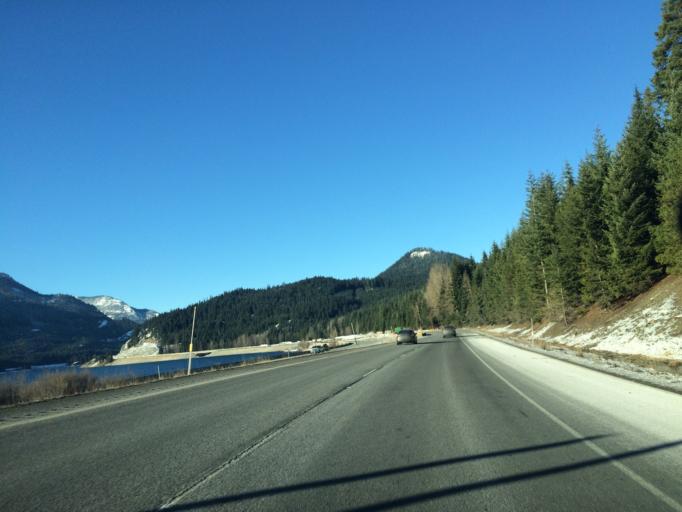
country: US
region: Washington
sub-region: King County
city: Tanner
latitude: 47.3322
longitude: -121.3449
